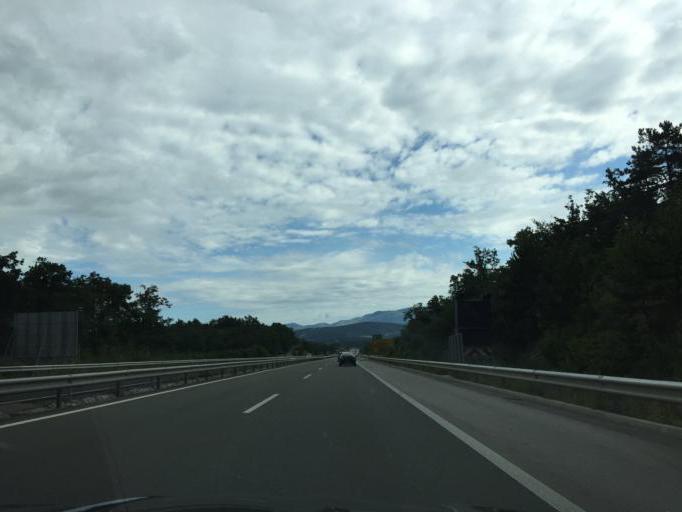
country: SI
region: Divaca
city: Divaca
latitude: 45.6617
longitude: 13.9651
